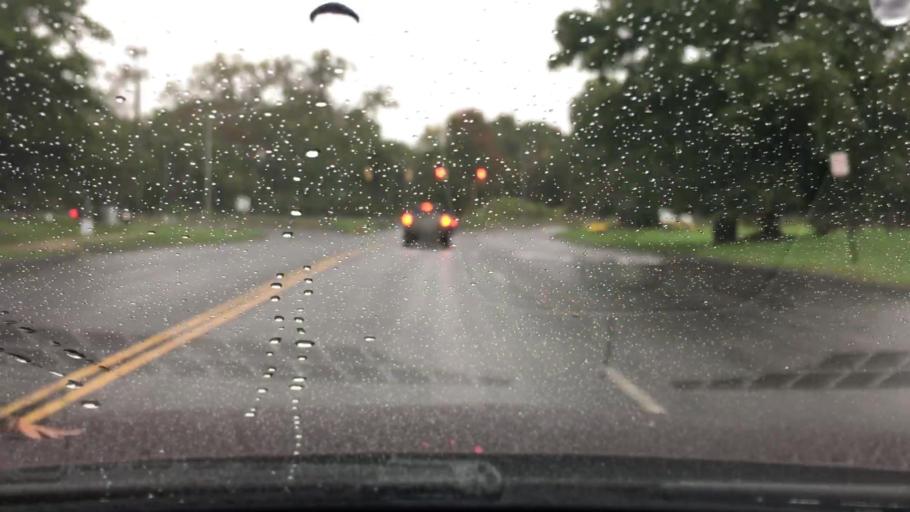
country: US
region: Connecticut
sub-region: Middlesex County
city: Cromwell
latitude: 41.6504
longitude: -72.6674
